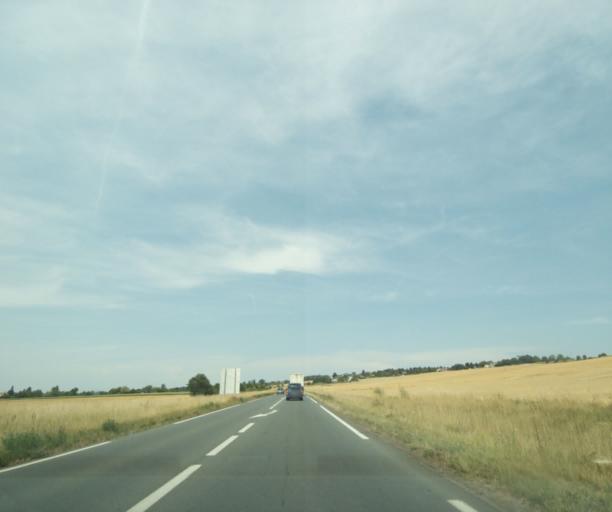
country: FR
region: Poitou-Charentes
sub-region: Departement de la Vienne
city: Chatellerault
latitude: 46.8005
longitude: 0.5623
